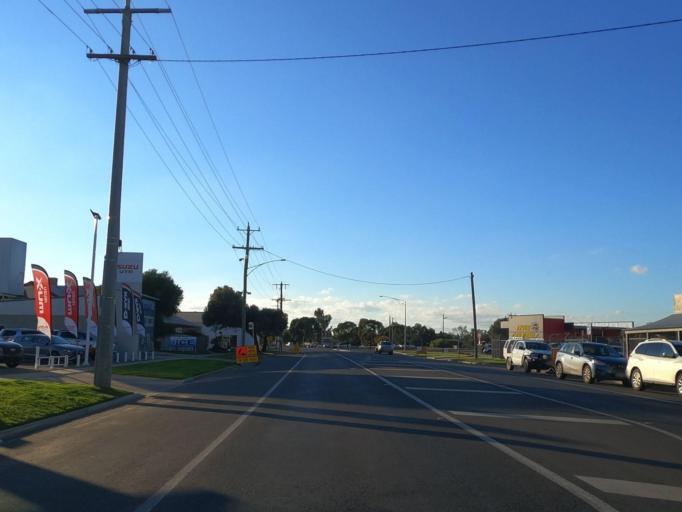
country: AU
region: Victoria
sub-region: Swan Hill
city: Swan Hill
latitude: -35.3359
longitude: 143.5601
